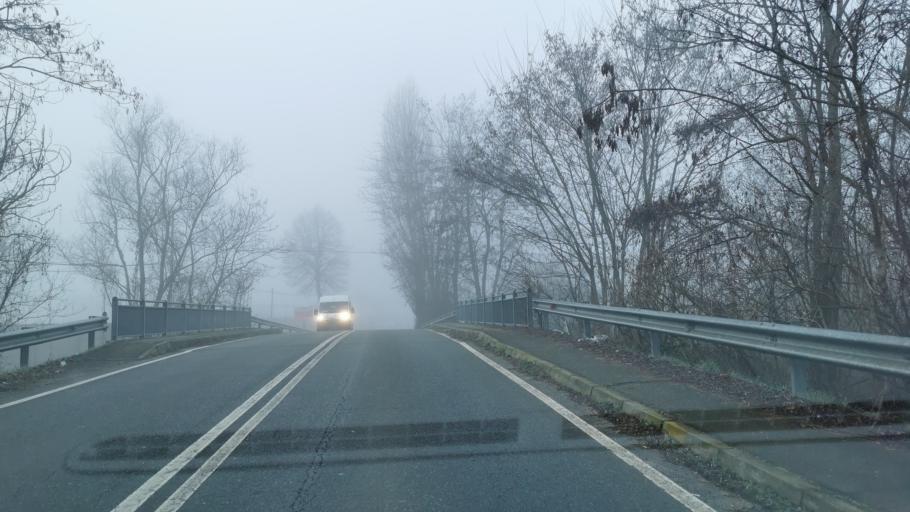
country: IT
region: Piedmont
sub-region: Provincia di Torino
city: Volpiano
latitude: 45.1925
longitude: 7.7542
